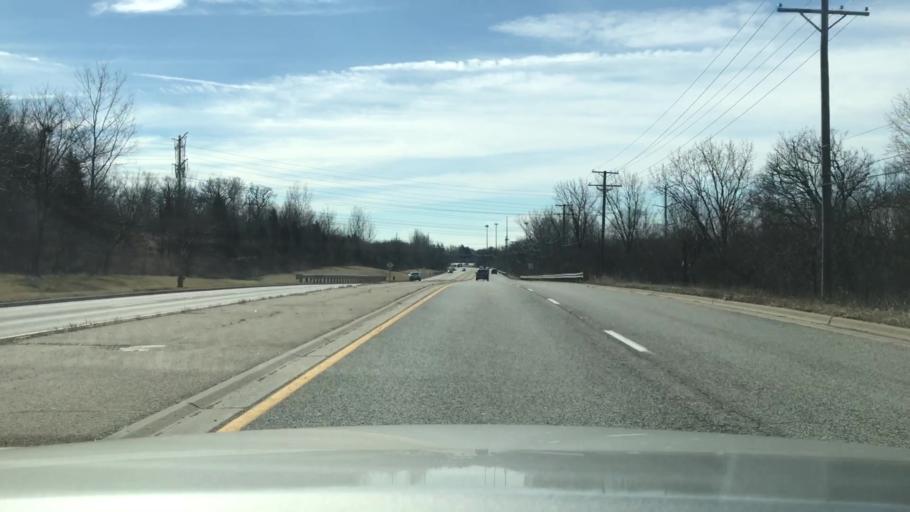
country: US
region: Illinois
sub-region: DuPage County
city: Woodridge
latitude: 41.7565
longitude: -88.0649
